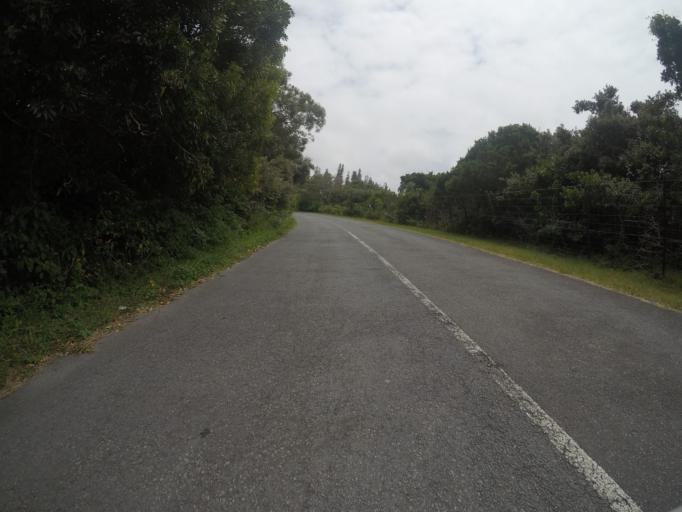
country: ZA
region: Eastern Cape
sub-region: Buffalo City Metropolitan Municipality
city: East London
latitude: -32.9944
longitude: 27.9392
